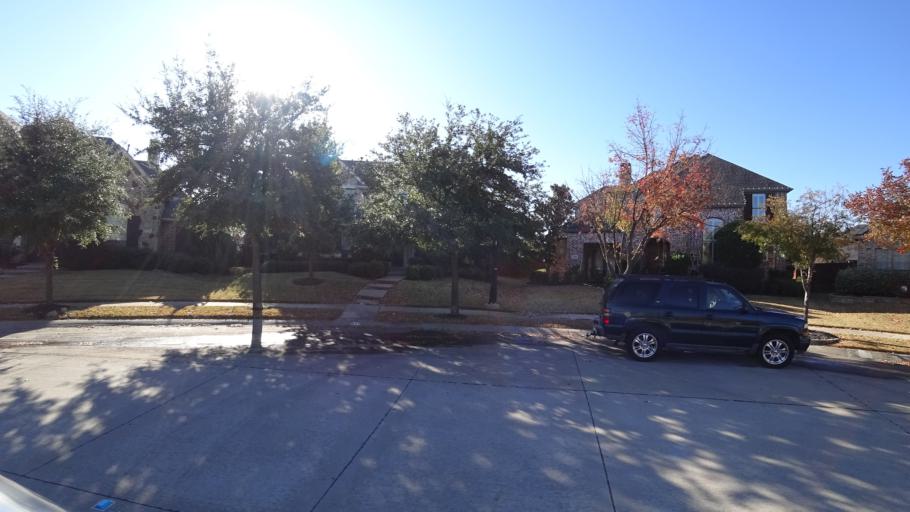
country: US
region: Texas
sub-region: Denton County
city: The Colony
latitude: 33.0432
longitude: -96.9139
